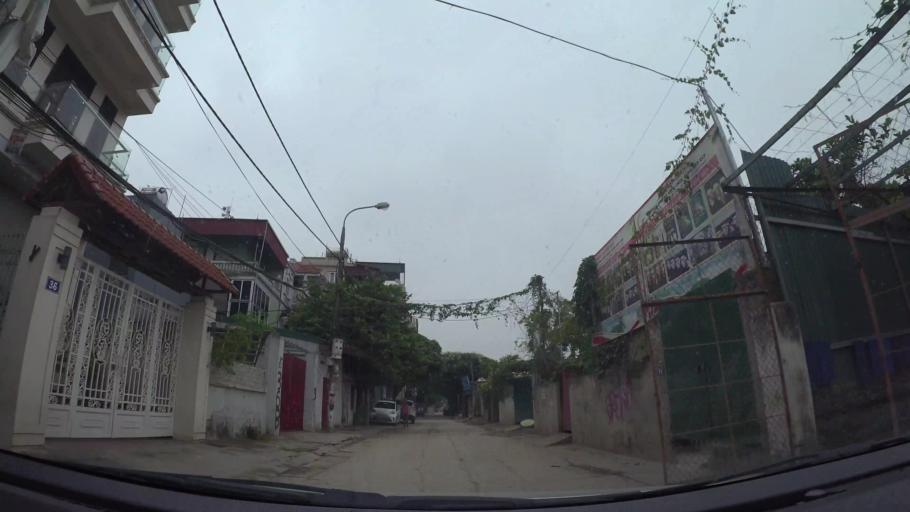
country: VN
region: Ha Noi
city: Tay Ho
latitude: 21.0660
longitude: 105.8367
